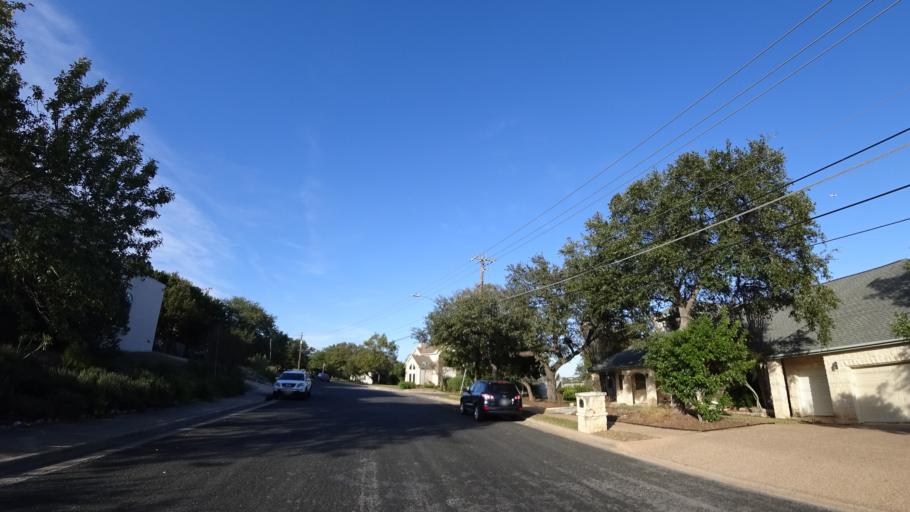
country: US
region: Texas
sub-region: Williamson County
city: Jollyville
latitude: 30.3966
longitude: -97.7661
